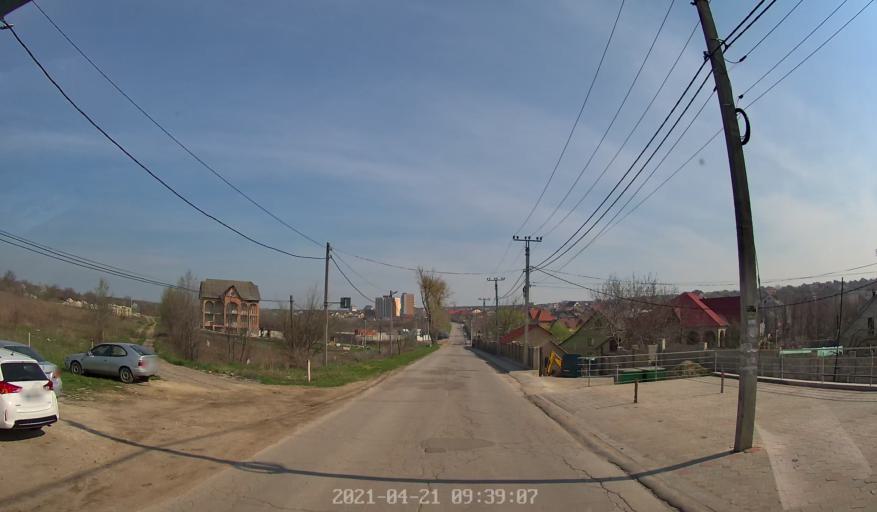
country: MD
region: Chisinau
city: Chisinau
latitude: 46.9871
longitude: 28.9325
